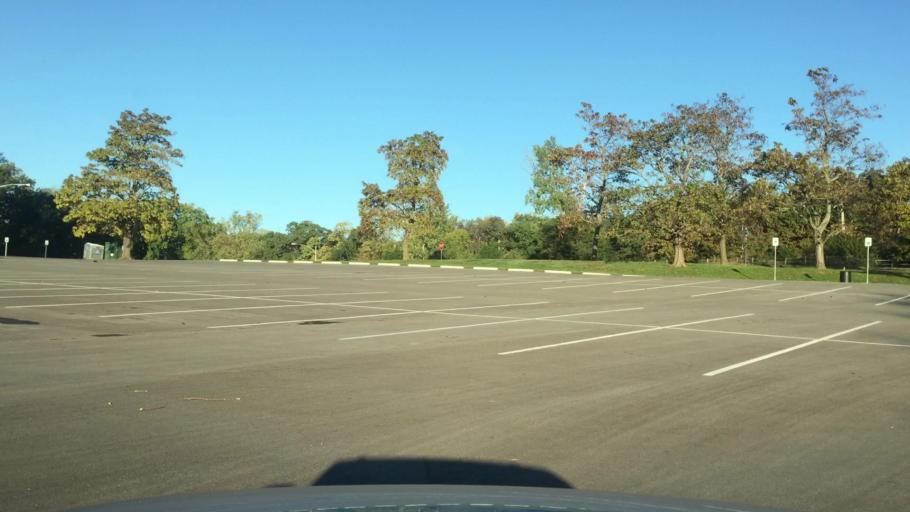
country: US
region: Kansas
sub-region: Johnson County
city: Lenexa
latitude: 38.9874
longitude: -94.7998
